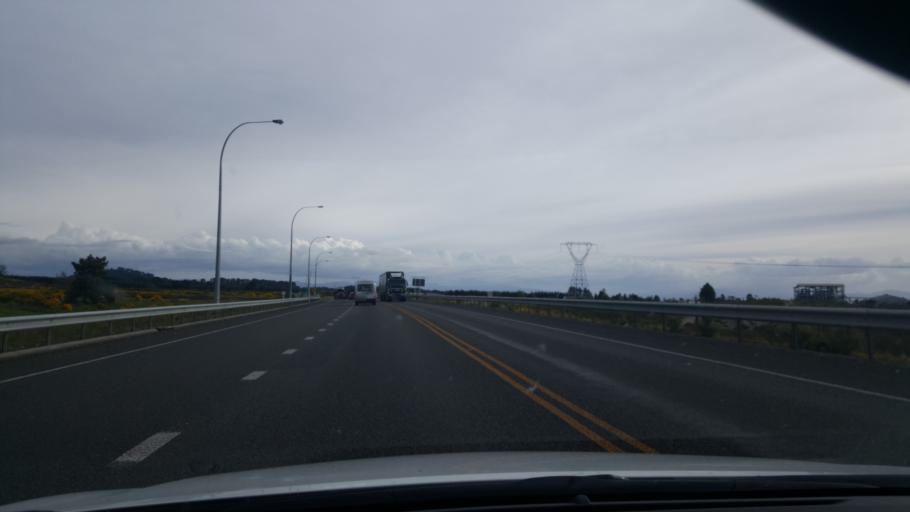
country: NZ
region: Waikato
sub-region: Taupo District
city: Taupo
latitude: -38.6846
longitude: 176.1142
